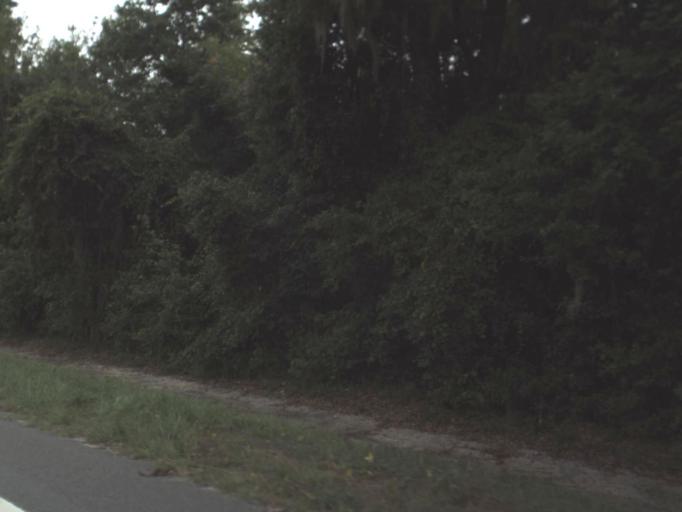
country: US
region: Florida
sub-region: Madison County
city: Madison
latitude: 30.6098
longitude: -83.3422
